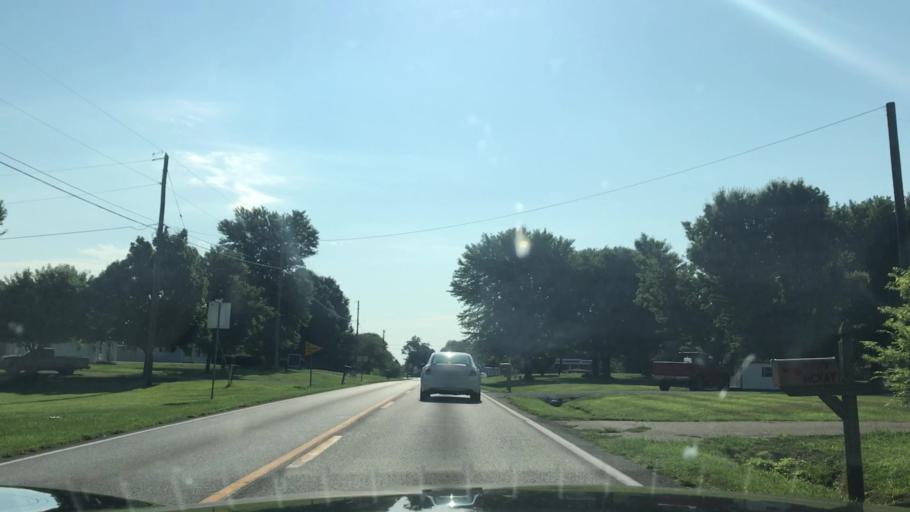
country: US
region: Kentucky
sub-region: Hart County
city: Horse Cave
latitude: 37.1667
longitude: -85.8425
